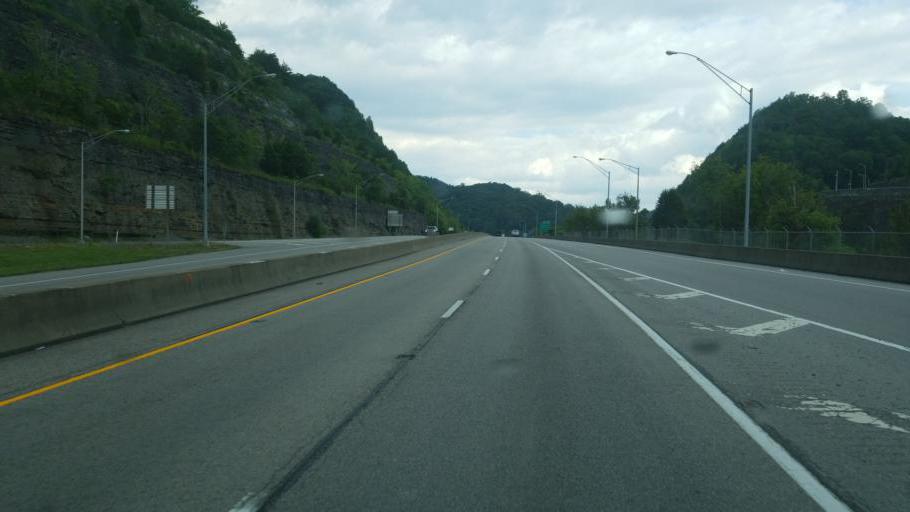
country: US
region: Kentucky
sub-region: Pike County
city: Pikeville
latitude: 37.4784
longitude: -82.5419
